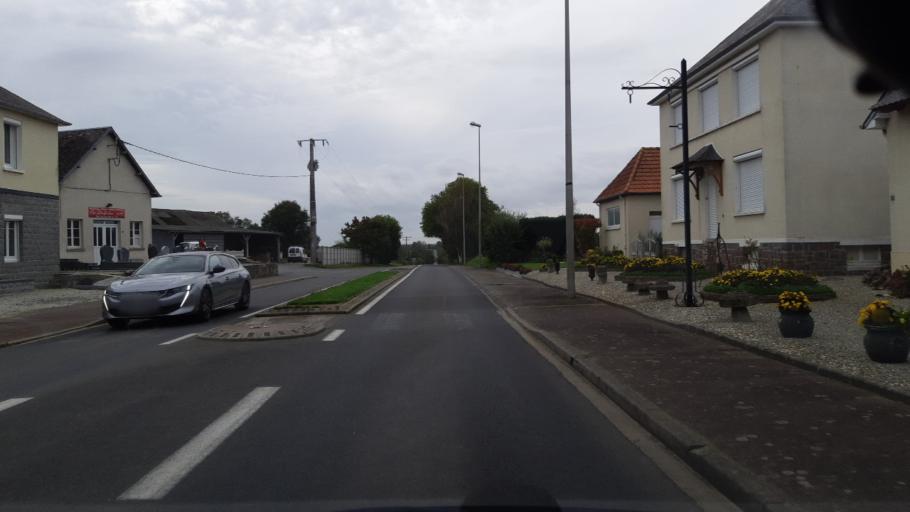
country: FR
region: Lower Normandy
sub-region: Departement de la Manche
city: Hambye
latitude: 48.9466
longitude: -1.2778
